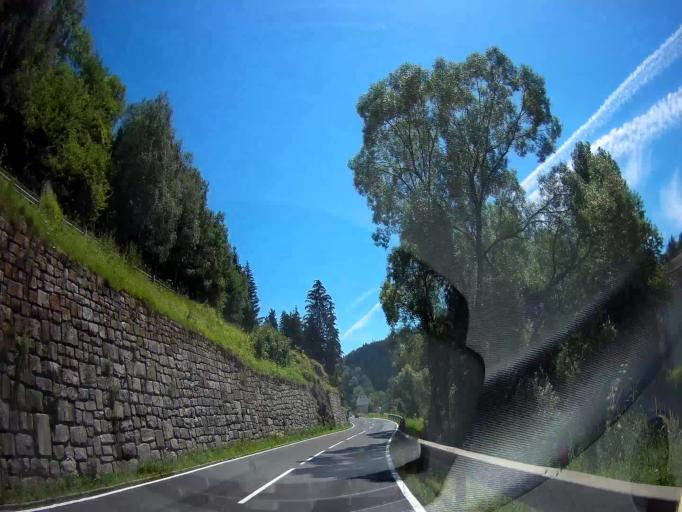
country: AT
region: Carinthia
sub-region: Politischer Bezirk Sankt Veit an der Glan
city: Micheldorf
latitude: 46.8988
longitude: 14.4422
